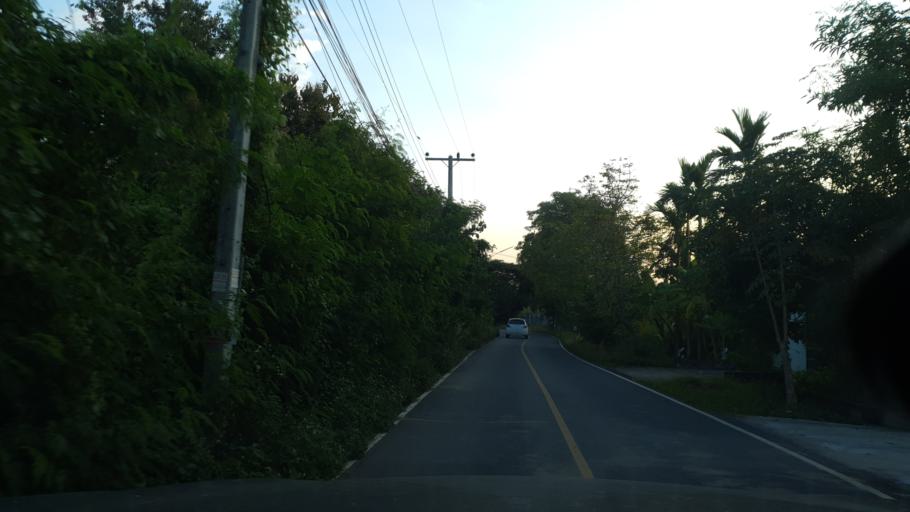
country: TH
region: Chiang Mai
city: San Sai
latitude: 18.8558
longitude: 99.0742
